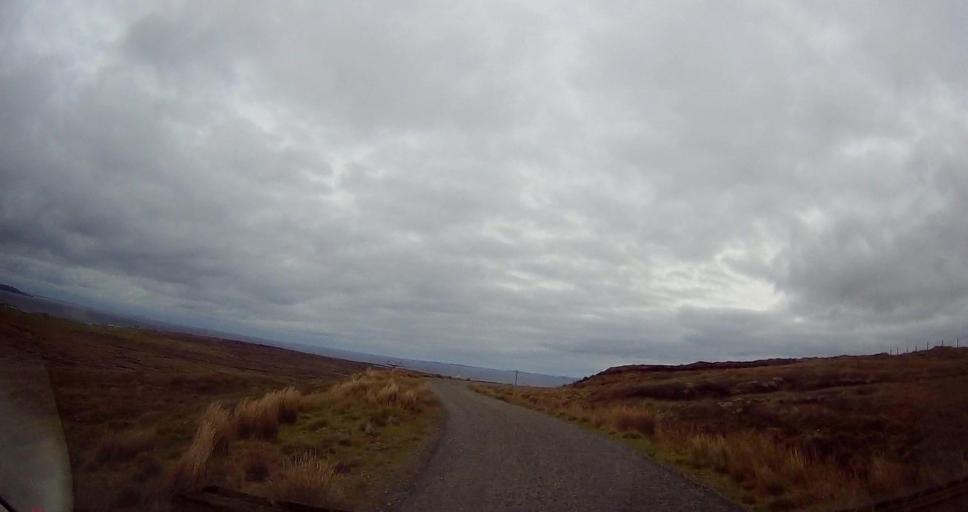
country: GB
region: Scotland
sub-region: Shetland Islands
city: Shetland
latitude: 60.5624
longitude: -1.0635
